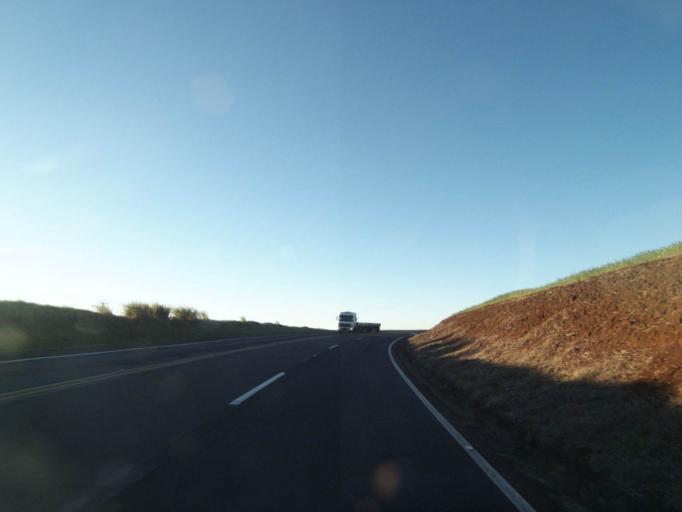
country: BR
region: Parana
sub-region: Faxinal
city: Faxinal
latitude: -23.8249
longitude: -51.1681
